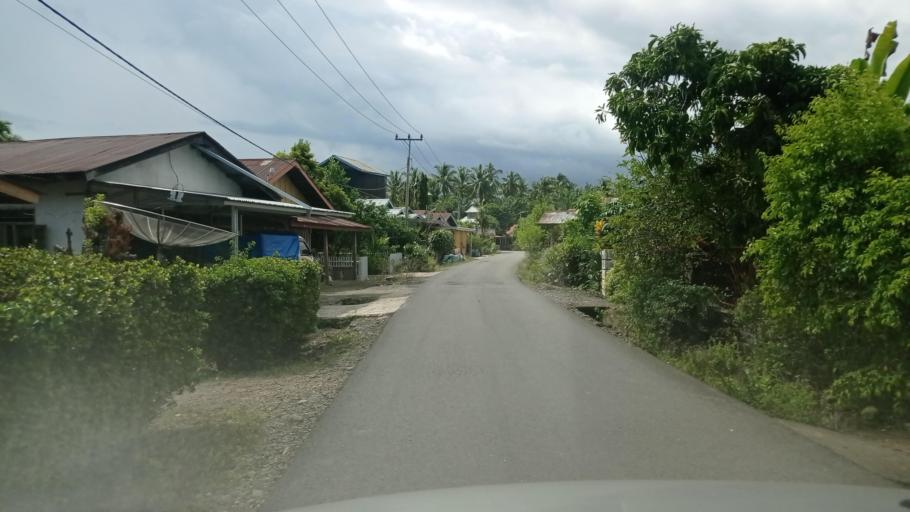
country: ID
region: Jambi
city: Sungai Penuh
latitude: -2.4790
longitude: 101.0958
